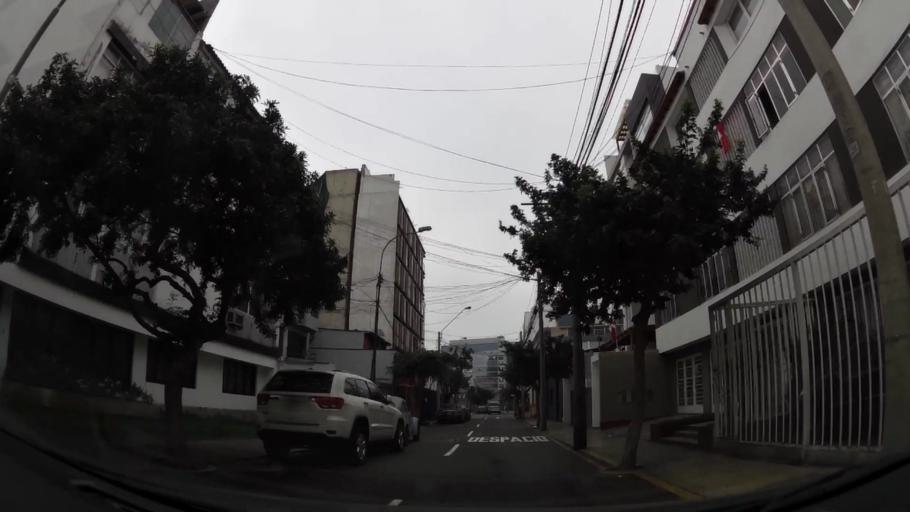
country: PE
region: Lima
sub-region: Lima
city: San Isidro
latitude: -12.1267
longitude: -77.0322
